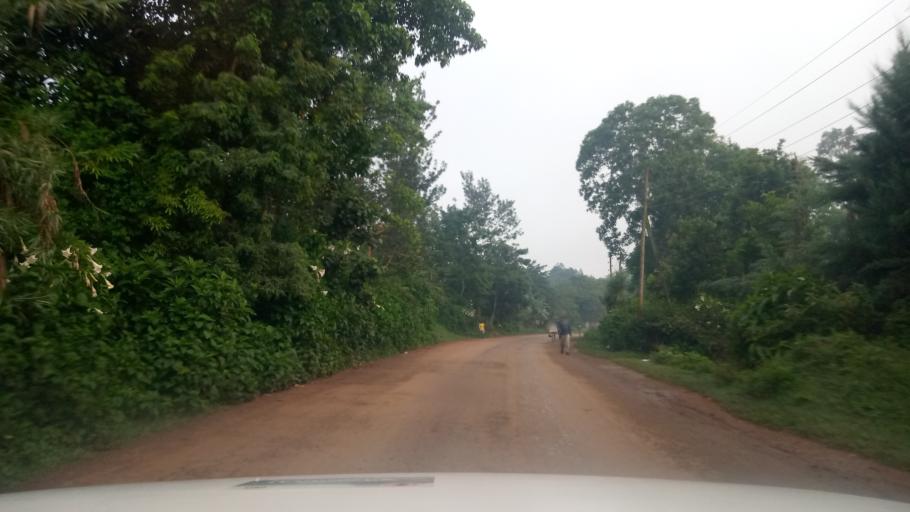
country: ET
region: Oromiya
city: Jima
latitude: 7.6879
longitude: 36.8281
